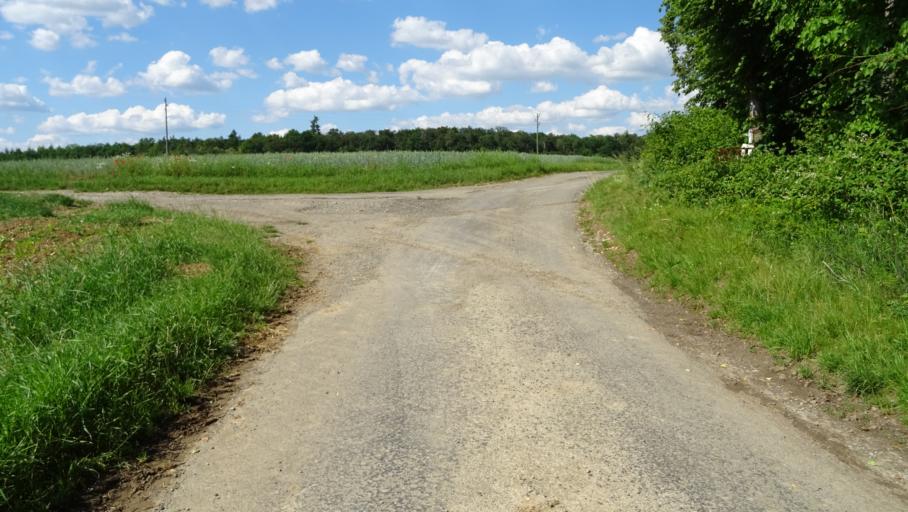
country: DE
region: Baden-Wuerttemberg
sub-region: Karlsruhe Region
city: Adelsheim
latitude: 49.4161
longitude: 9.3676
